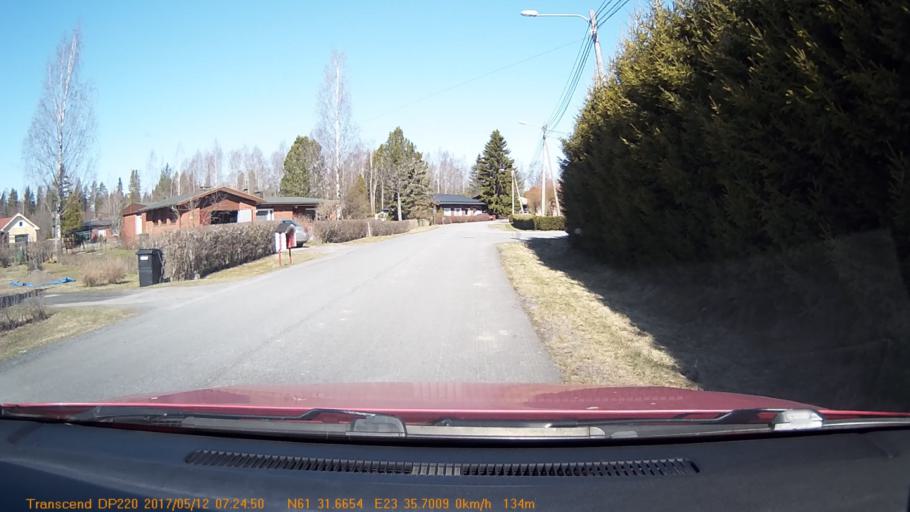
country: FI
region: Pirkanmaa
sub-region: Tampere
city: Yloejaervi
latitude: 61.5278
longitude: 23.5950
